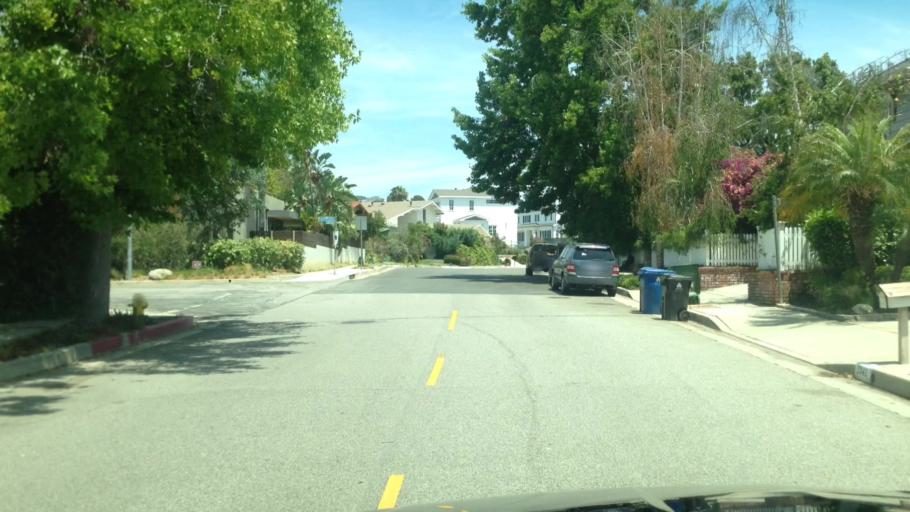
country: US
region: California
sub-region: Los Angeles County
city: Santa Monica
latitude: 34.0783
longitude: -118.5063
